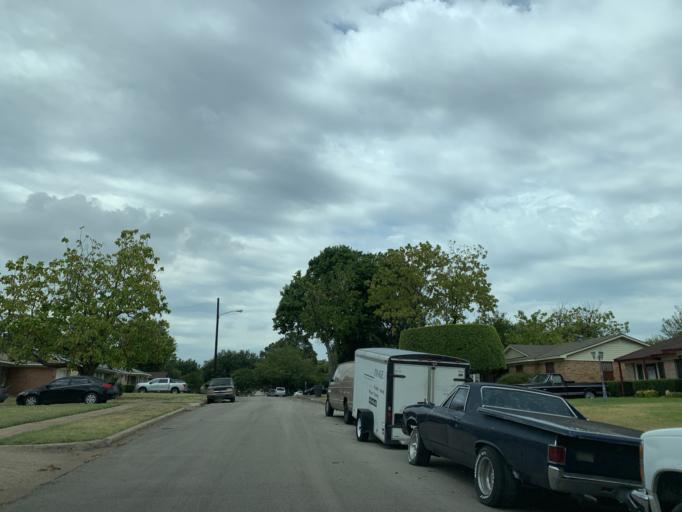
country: US
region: Texas
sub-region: Dallas County
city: DeSoto
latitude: 32.6556
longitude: -96.8320
